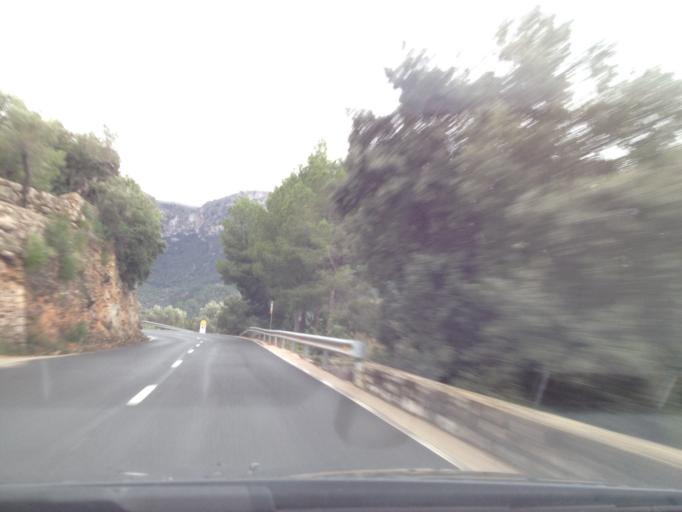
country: ES
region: Balearic Islands
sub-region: Illes Balears
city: Deia
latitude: 39.7570
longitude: 2.6469
